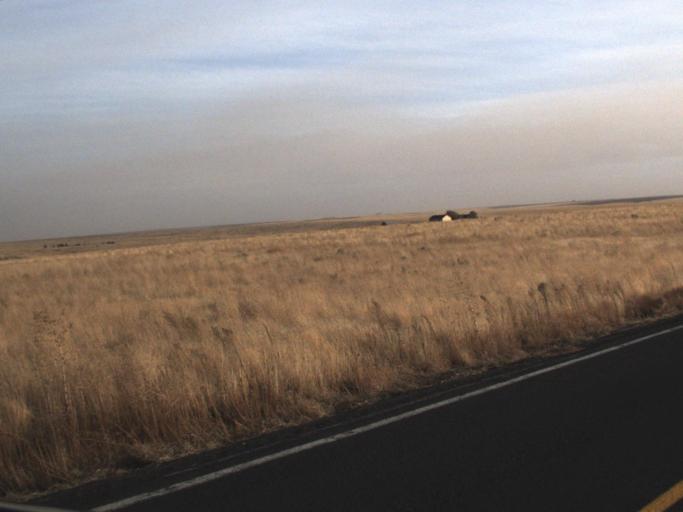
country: US
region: Washington
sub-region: Adams County
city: Ritzville
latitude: 47.2574
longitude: -118.6859
